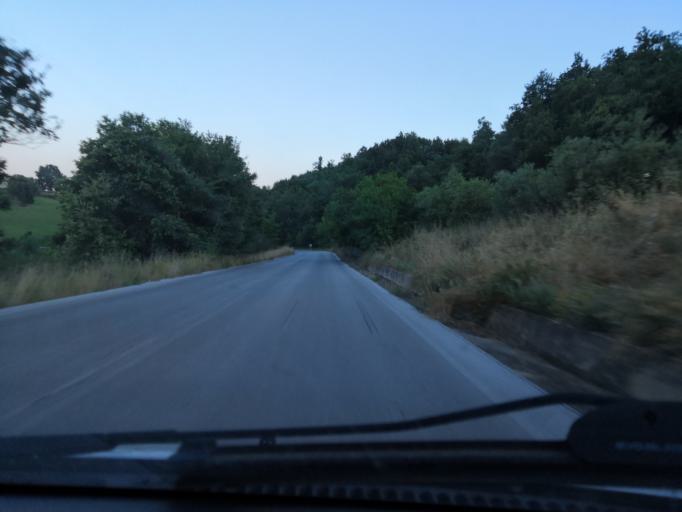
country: IT
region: Molise
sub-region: Provincia di Campobasso
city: Jelsi
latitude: 41.5113
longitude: 14.7747
